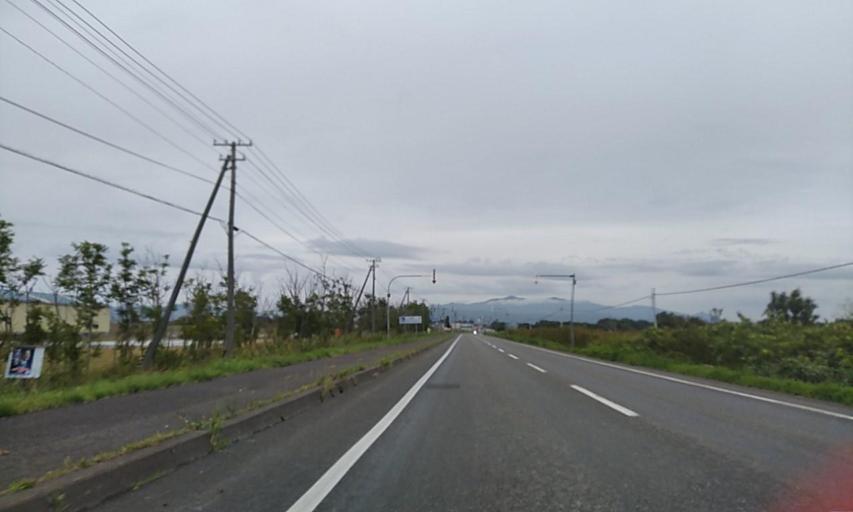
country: JP
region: Hokkaido
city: Makubetsu
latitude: 45.1393
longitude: 142.3625
